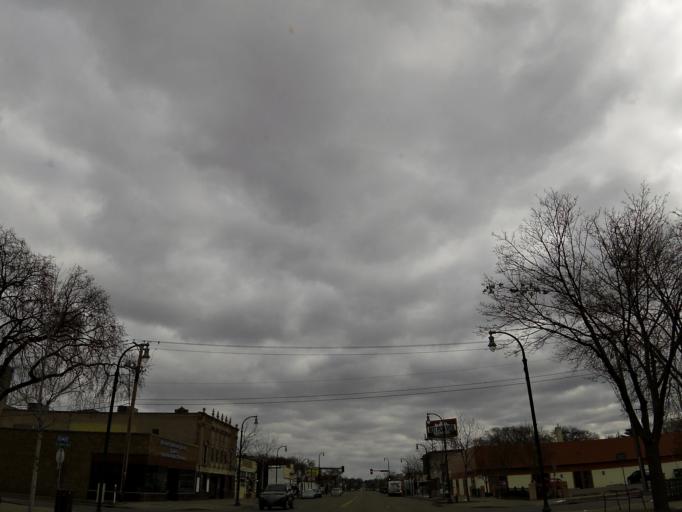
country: US
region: Minnesota
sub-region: Hennepin County
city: Minneapolis
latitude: 44.9484
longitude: -93.2221
